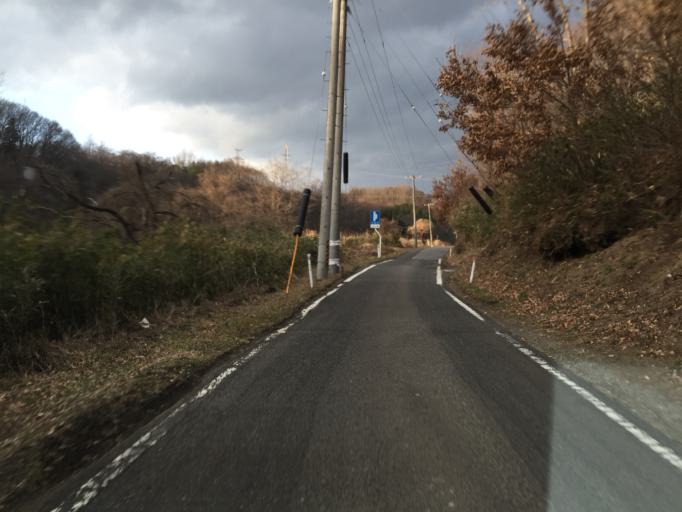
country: JP
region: Fukushima
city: Motomiya
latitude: 37.5304
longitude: 140.4145
